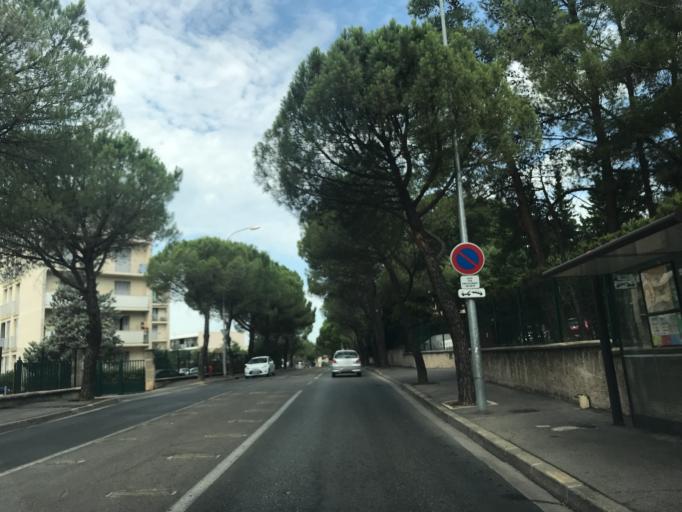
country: FR
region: Provence-Alpes-Cote d'Azur
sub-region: Departement des Bouches-du-Rhone
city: Aix-en-Provence
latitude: 43.5145
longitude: 5.4385
